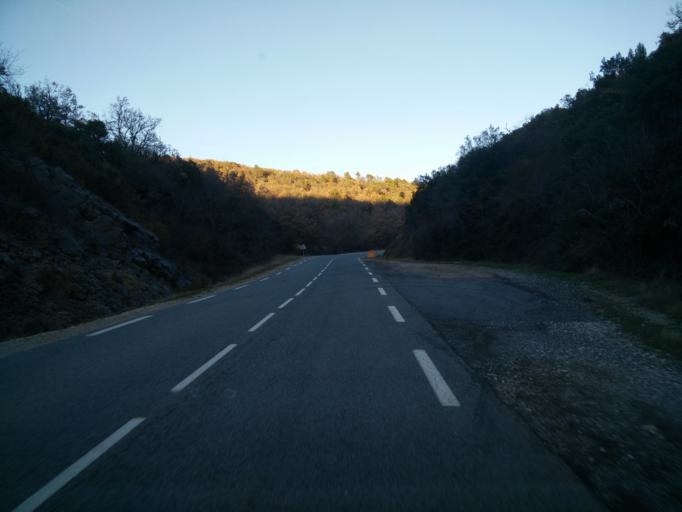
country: FR
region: Provence-Alpes-Cote d'Azur
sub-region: Departement du Var
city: Montferrat
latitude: 43.6244
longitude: 6.4829
